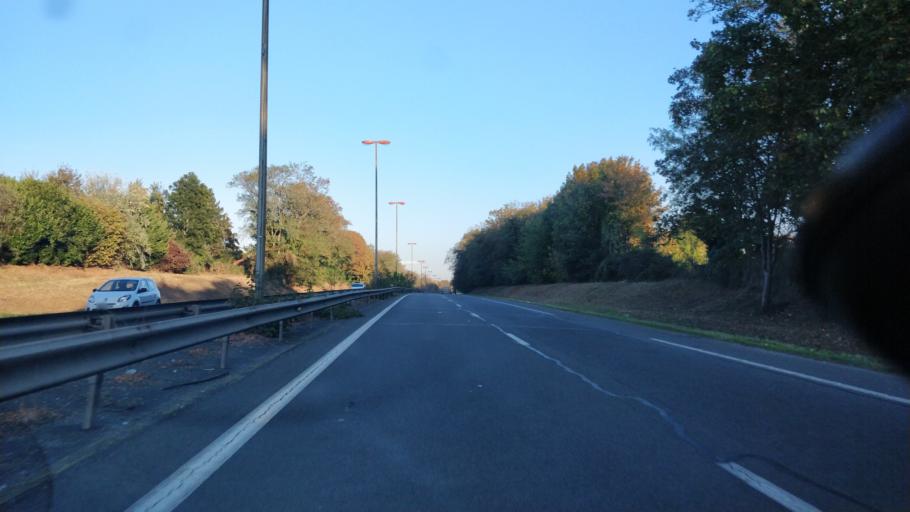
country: FR
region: Ile-de-France
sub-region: Departement de Seine-et-Marne
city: Champs-sur-Marne
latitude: 48.8485
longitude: 2.6087
